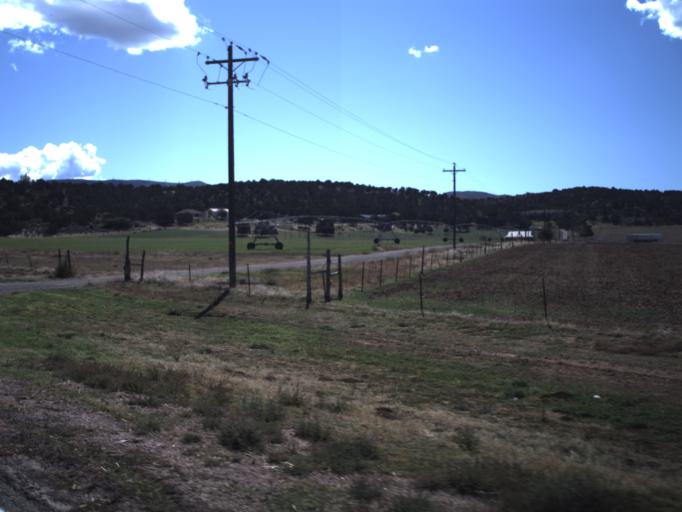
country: US
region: Utah
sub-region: Washington County
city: Enterprise
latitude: 37.5687
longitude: -113.6985
